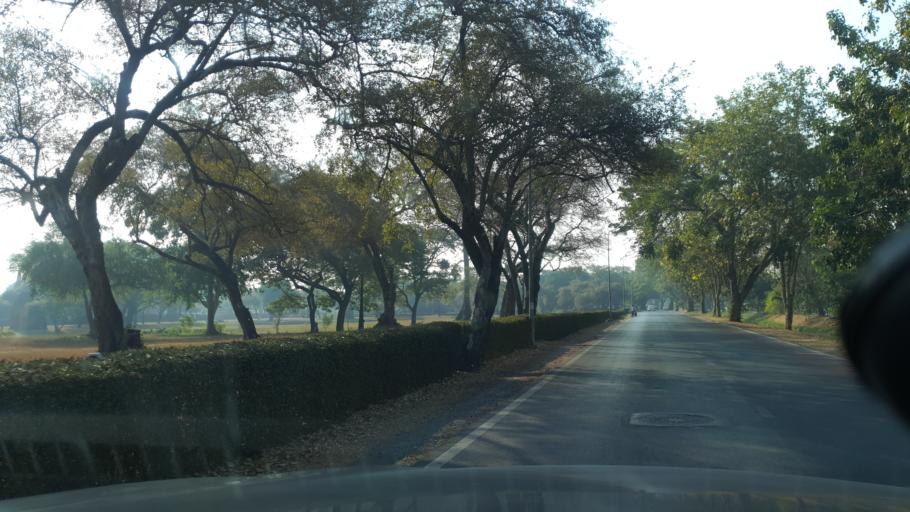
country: TH
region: Phra Nakhon Si Ayutthaya
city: Phra Nakhon Si Ayutthaya
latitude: 14.3573
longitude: 100.5556
